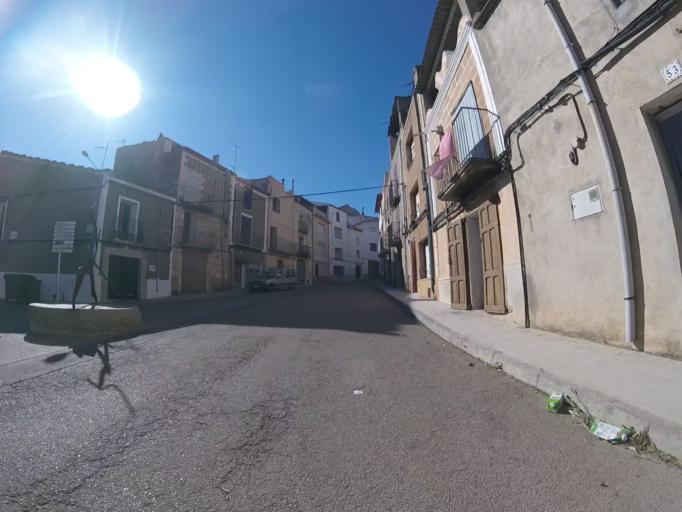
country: ES
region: Valencia
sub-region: Provincia de Castello
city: Cati
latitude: 40.4246
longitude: 0.0785
